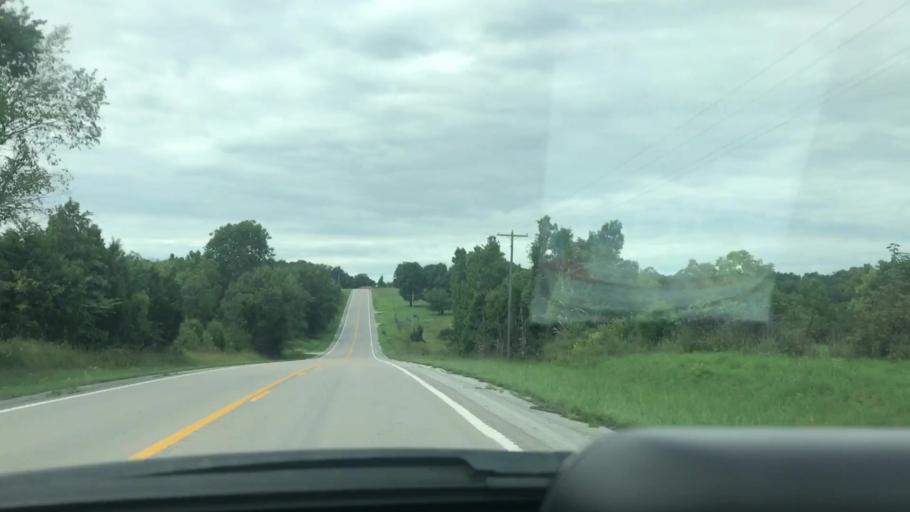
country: US
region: Missouri
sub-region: Benton County
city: Warsaw
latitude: 38.1492
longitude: -93.2929
